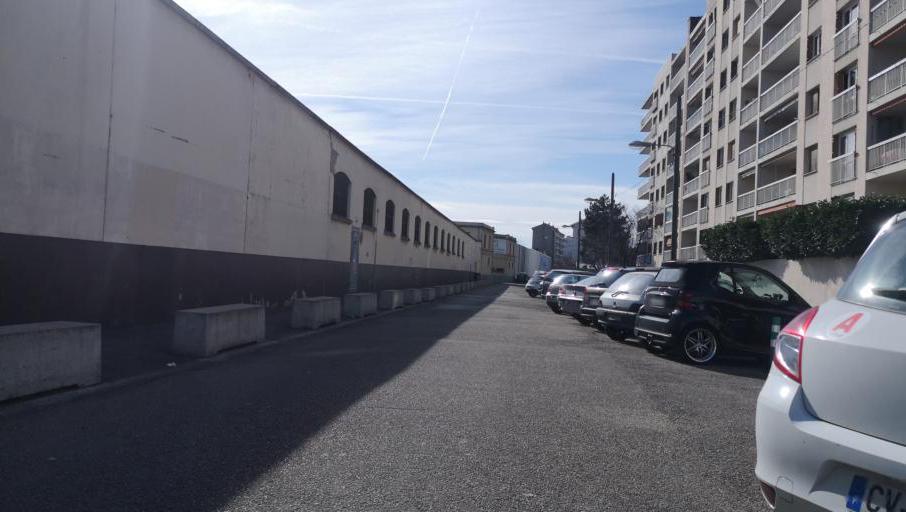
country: FR
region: Rhone-Alpes
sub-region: Departement du Rhone
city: Villeurbanne
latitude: 45.7773
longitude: 4.8792
